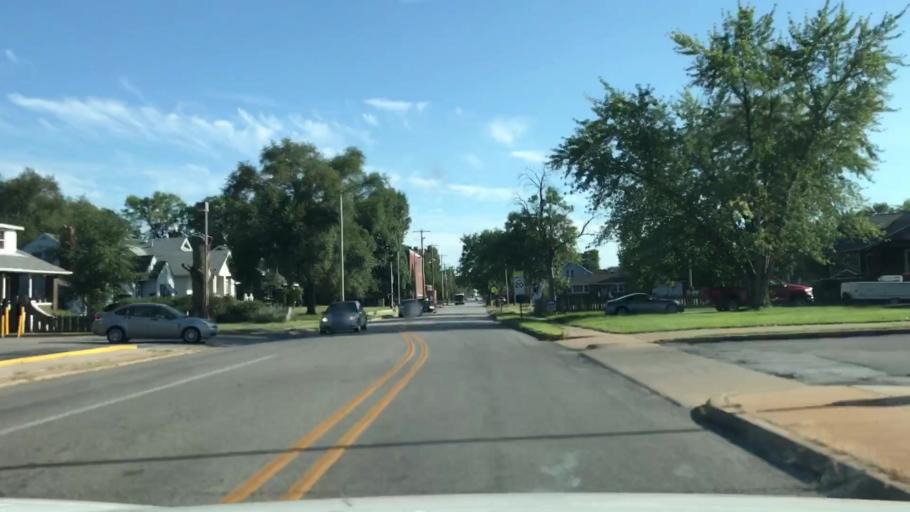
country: US
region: Illinois
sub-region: Madison County
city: Wood River
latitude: 38.8736
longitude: -90.0989
